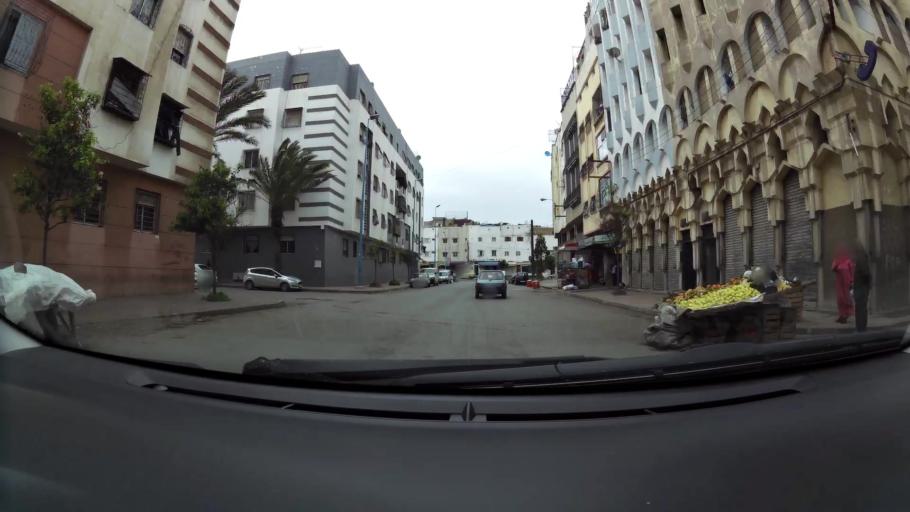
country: MA
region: Grand Casablanca
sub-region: Casablanca
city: Casablanca
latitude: 33.5753
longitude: -7.5690
